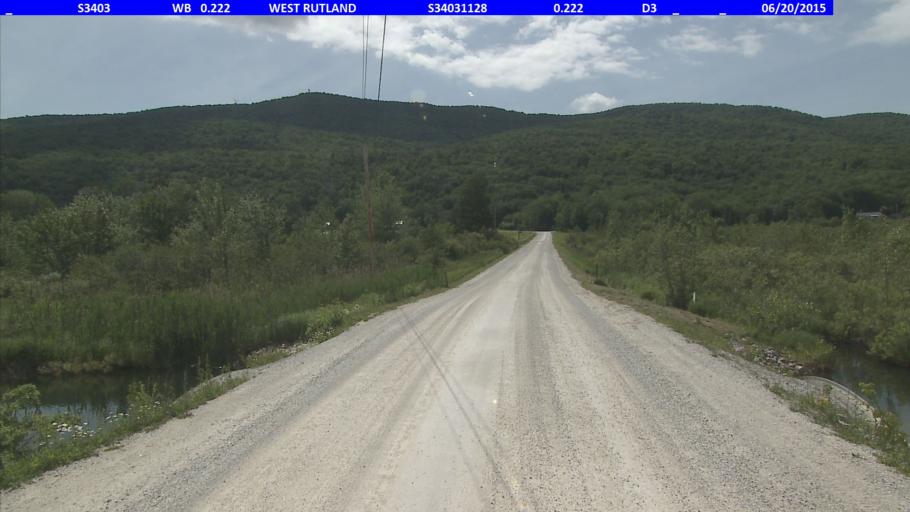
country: US
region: Vermont
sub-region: Rutland County
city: West Rutland
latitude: 43.6313
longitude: -73.0638
